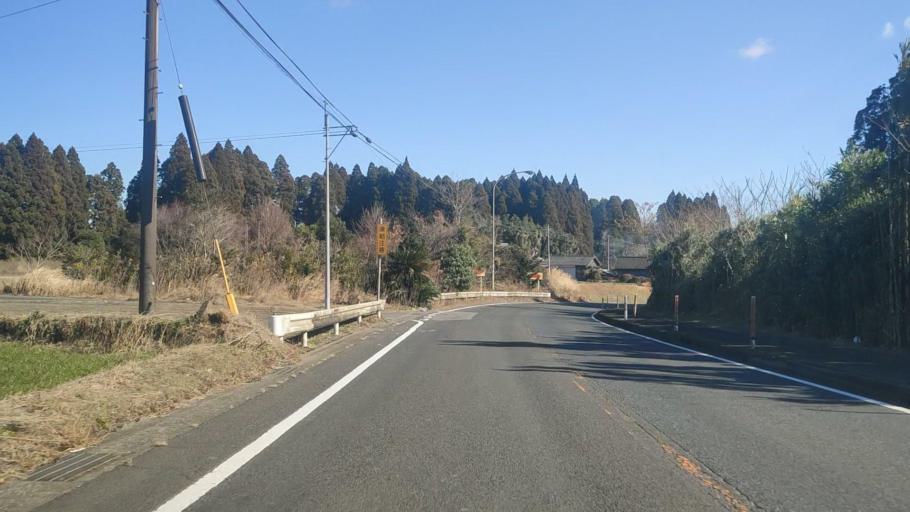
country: JP
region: Kagoshima
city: Sueyoshicho-ninokata
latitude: 31.6706
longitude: 130.9165
